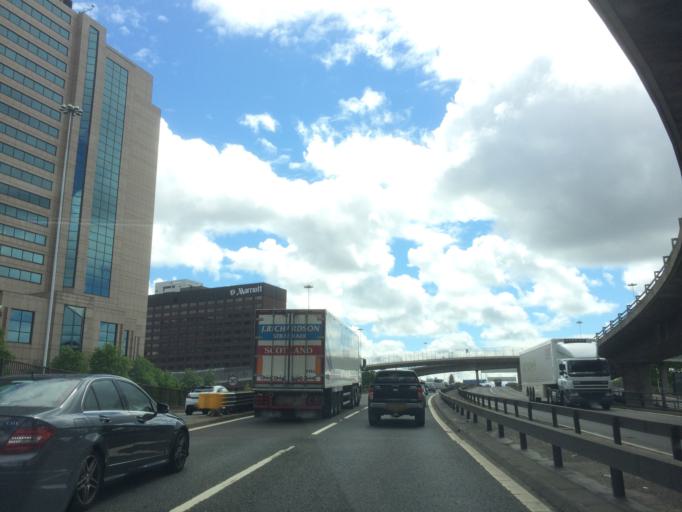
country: GB
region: Scotland
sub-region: Glasgow City
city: Glasgow
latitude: 55.8621
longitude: -4.2701
